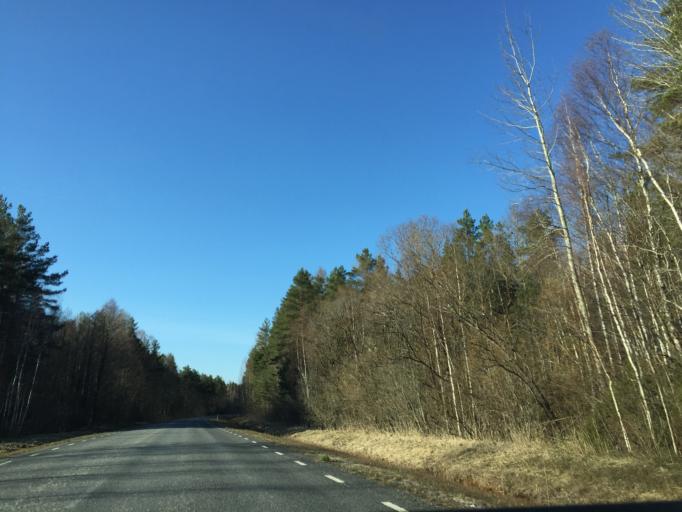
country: RU
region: Pskov
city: Gdov
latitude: 59.0511
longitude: 27.7029
